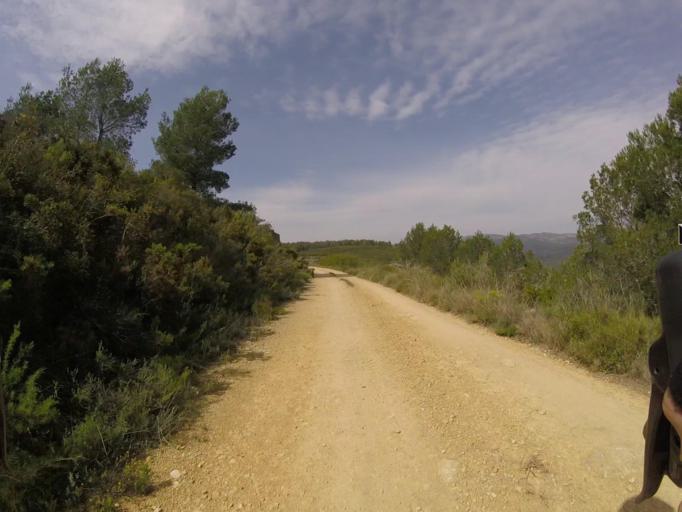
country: ES
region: Valencia
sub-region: Provincia de Castello
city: Cuevas de Vinroma
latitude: 40.2909
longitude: 0.1240
